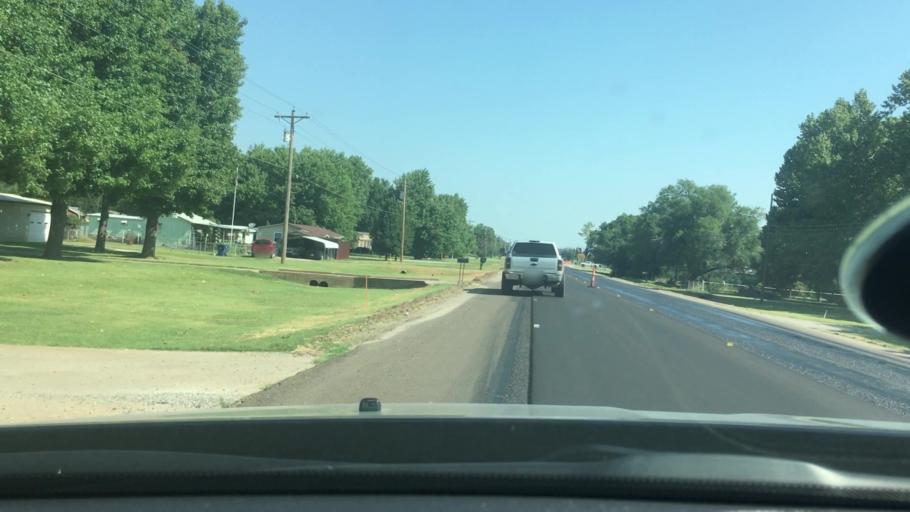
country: US
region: Oklahoma
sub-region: Garvin County
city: Lindsay
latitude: 34.8069
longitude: -97.5983
